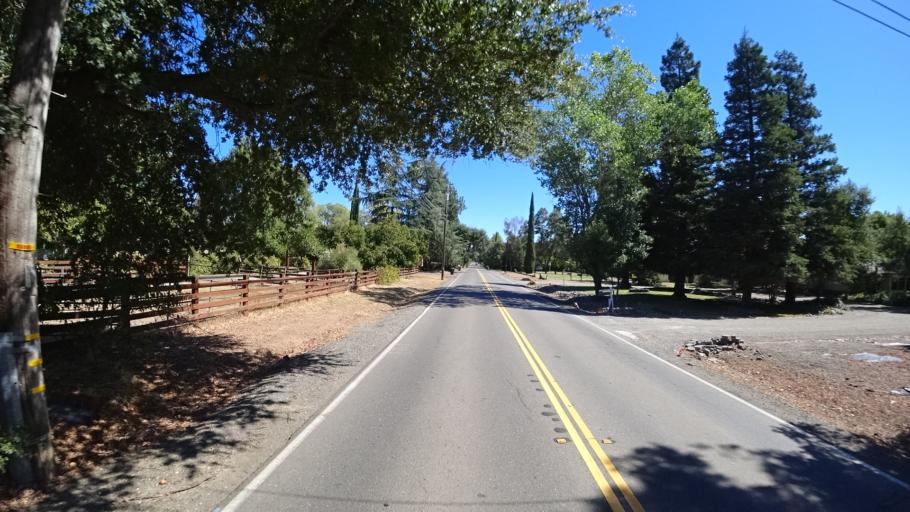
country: US
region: California
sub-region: Sacramento County
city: Vineyard
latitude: 38.4382
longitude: -121.3323
